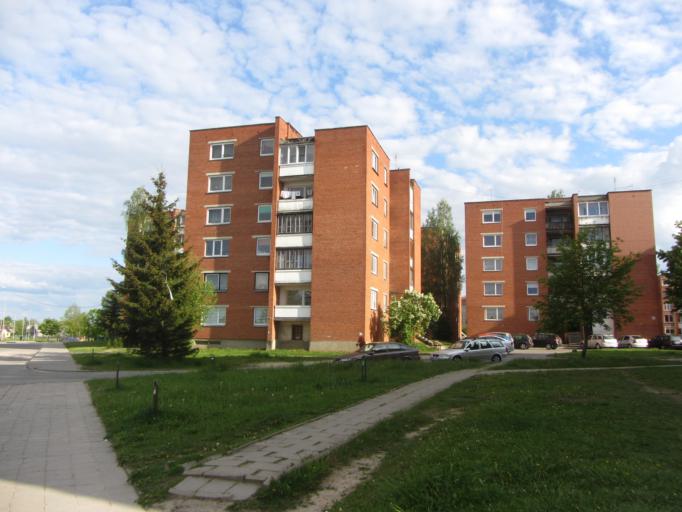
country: LT
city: Sirvintos
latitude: 55.0459
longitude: 24.9472
